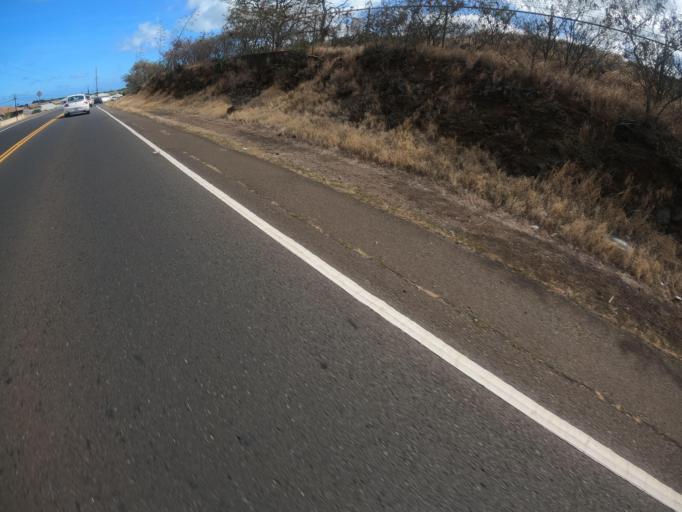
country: US
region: Hawaii
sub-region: Honolulu County
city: Makakilo City
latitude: 21.3377
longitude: -158.0739
